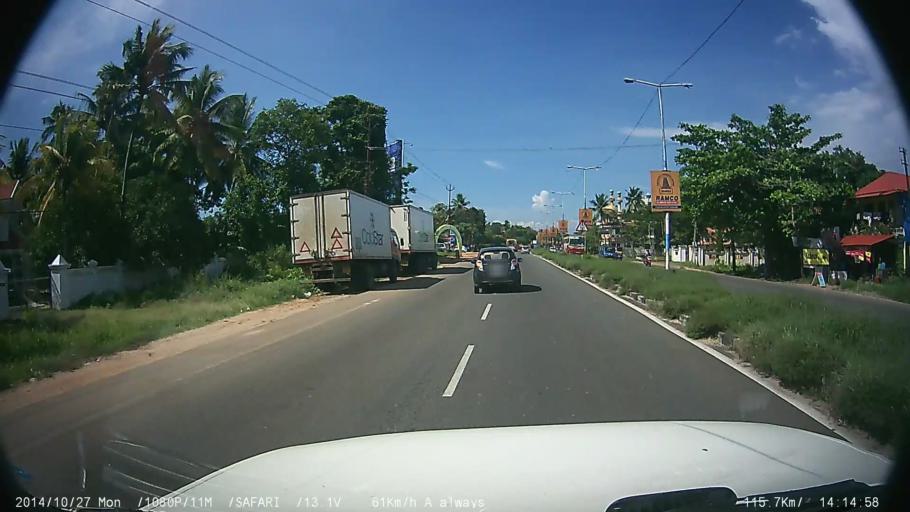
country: IN
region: Kerala
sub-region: Alappuzha
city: Kutiatodu
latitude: 9.8278
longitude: 76.3101
